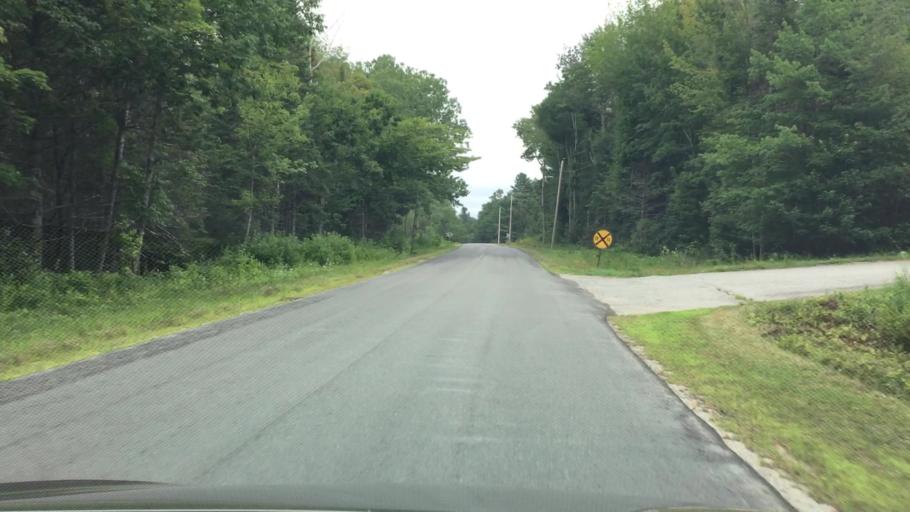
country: US
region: Maine
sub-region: Waldo County
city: Stockton Springs
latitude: 44.5301
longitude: -68.8366
